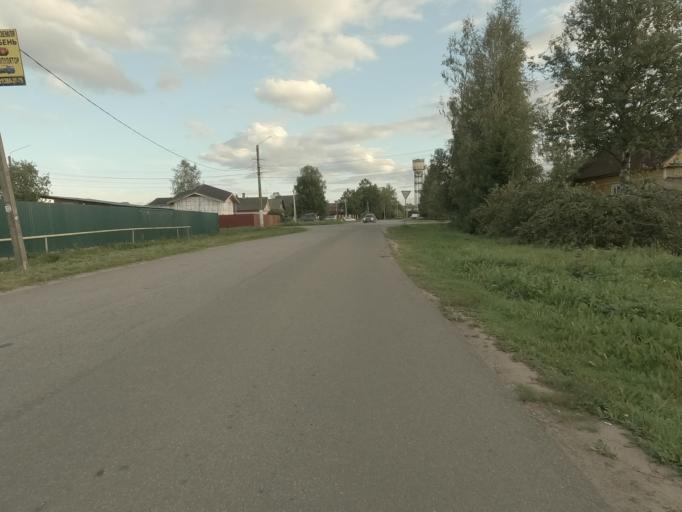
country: RU
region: Leningrad
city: Mga
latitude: 59.7578
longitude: 31.0766
